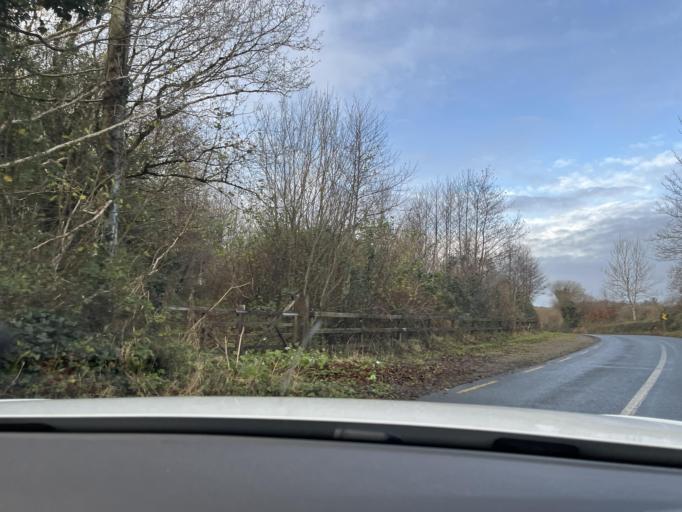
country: IE
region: Connaught
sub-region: Sligo
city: Sligo
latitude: 54.2644
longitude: -8.3624
